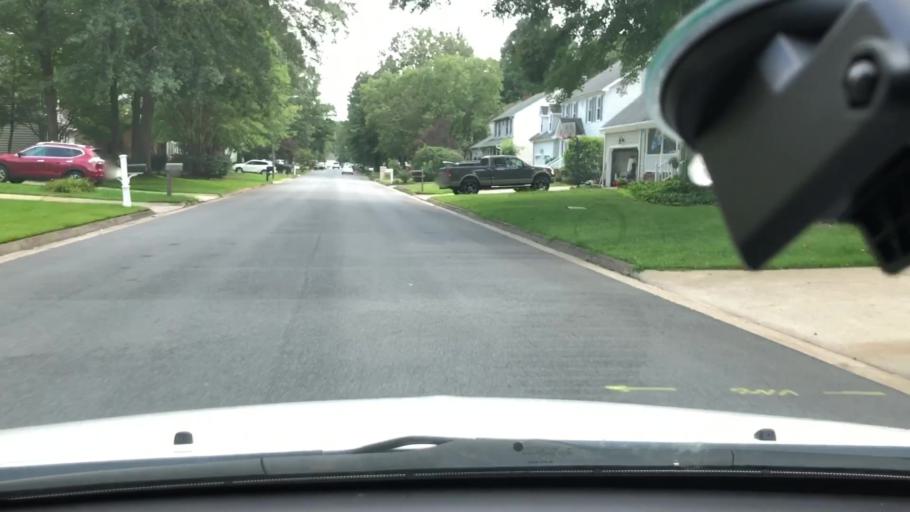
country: US
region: Virginia
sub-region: City of Chesapeake
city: Chesapeake
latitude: 36.7081
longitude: -76.2911
